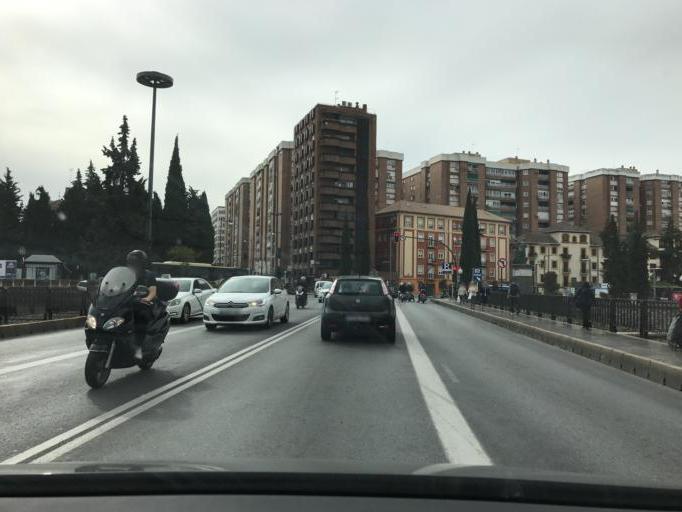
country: ES
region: Andalusia
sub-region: Provincia de Granada
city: Granada
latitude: 37.1685
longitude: -3.5965
